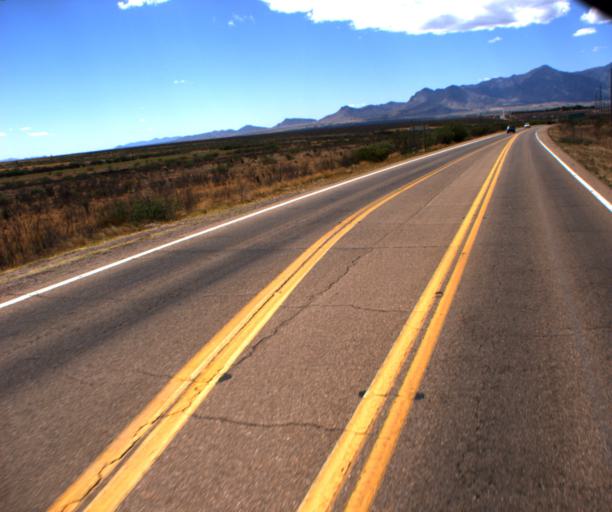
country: US
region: Arizona
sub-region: Cochise County
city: Naco
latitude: 31.3800
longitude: -110.0581
